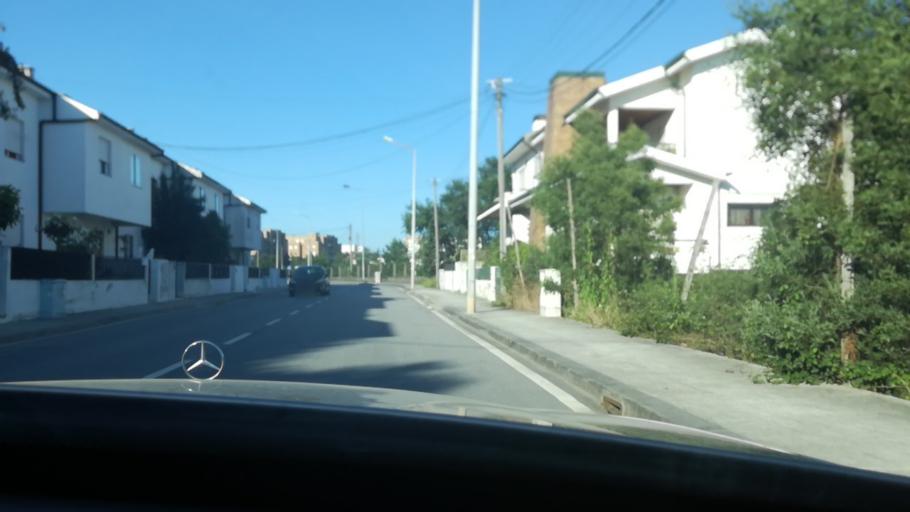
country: PT
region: Porto
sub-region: Maia
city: Leca do Bailio
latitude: 41.2233
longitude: -8.6223
